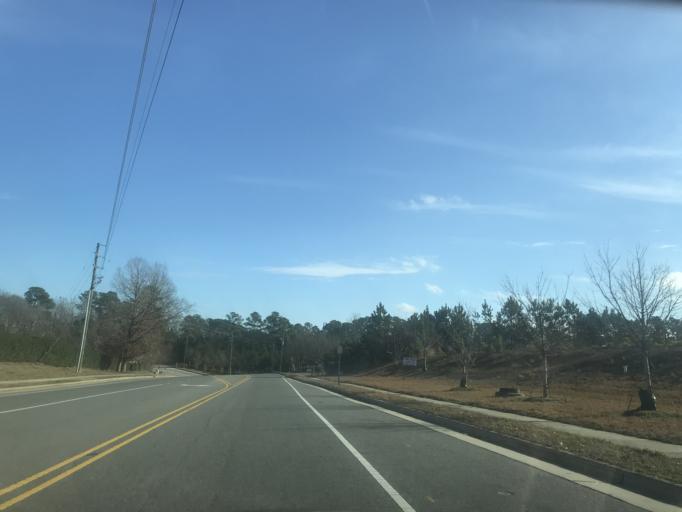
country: US
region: North Carolina
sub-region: Wake County
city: Garner
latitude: 35.7250
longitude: -78.5478
